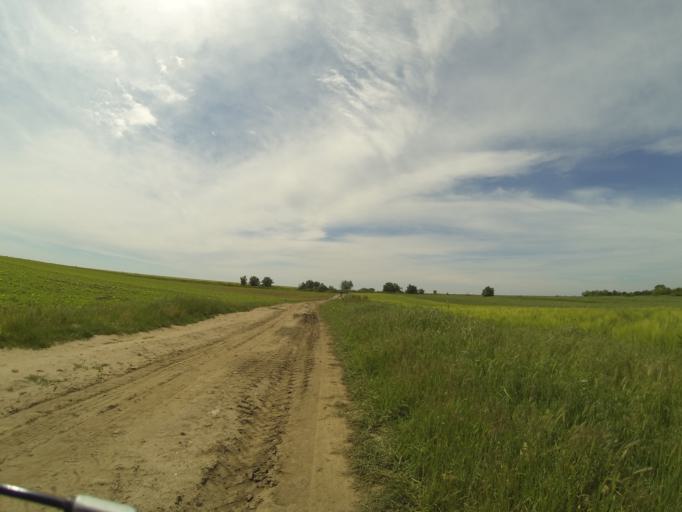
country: RO
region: Dolj
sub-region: Comuna Ghindeni
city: Ghindeni
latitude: 44.2085
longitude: 23.9385
